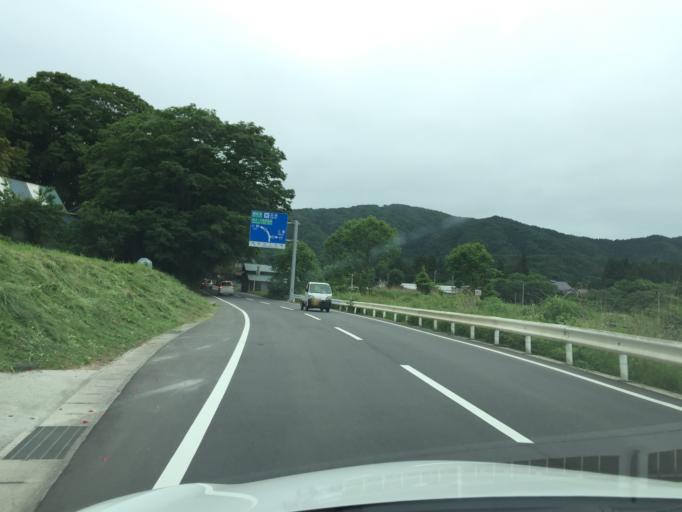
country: JP
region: Fukushima
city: Funehikimachi-funehiki
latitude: 37.3576
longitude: 140.6386
